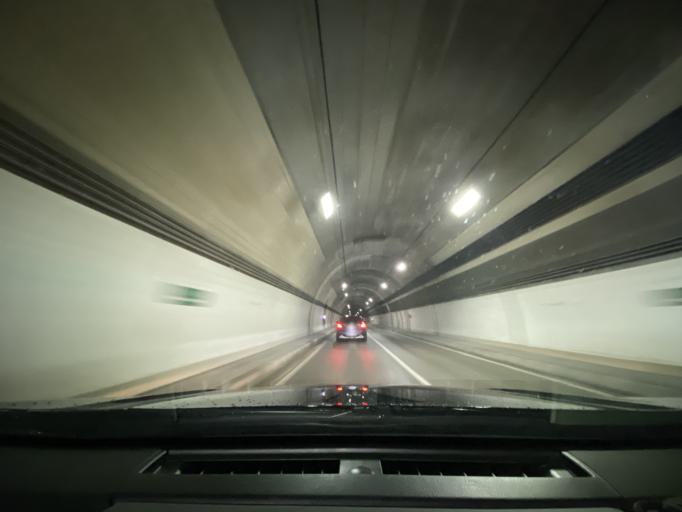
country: JP
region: Hokkaido
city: Ishikari
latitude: 43.4475
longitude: 141.4110
